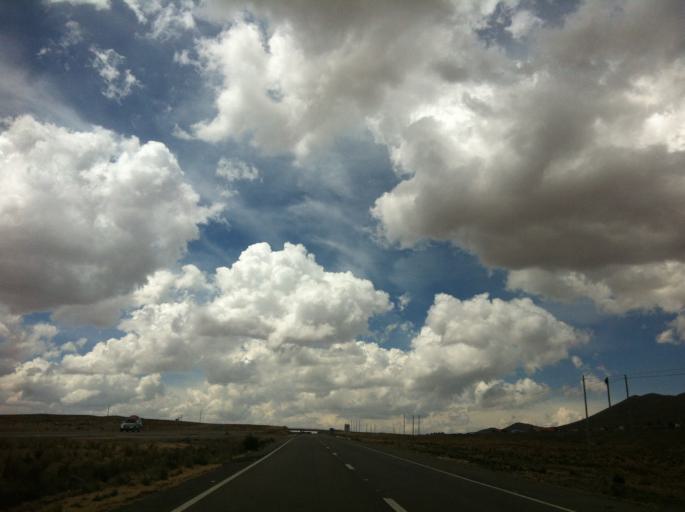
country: BO
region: La Paz
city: Patacamaya
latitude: -16.9201
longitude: -68.1143
